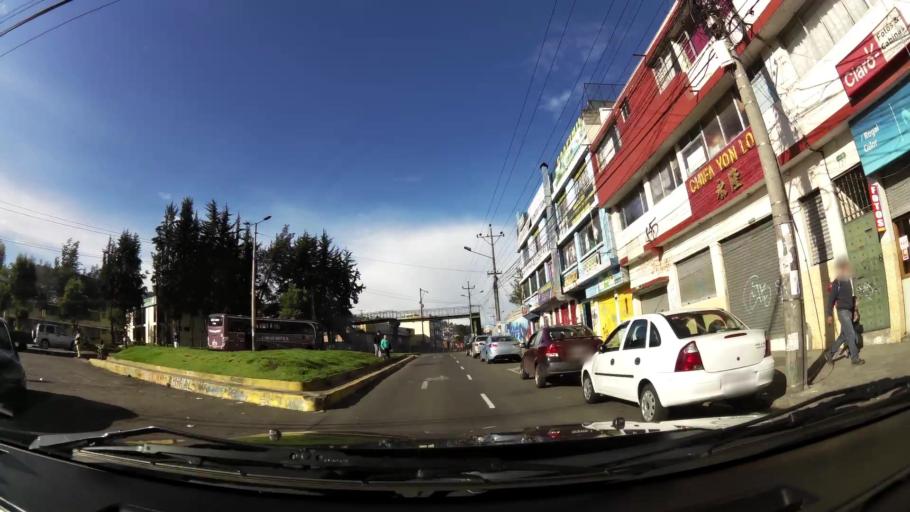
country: EC
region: Pichincha
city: Quito
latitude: -0.2665
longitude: -78.5271
